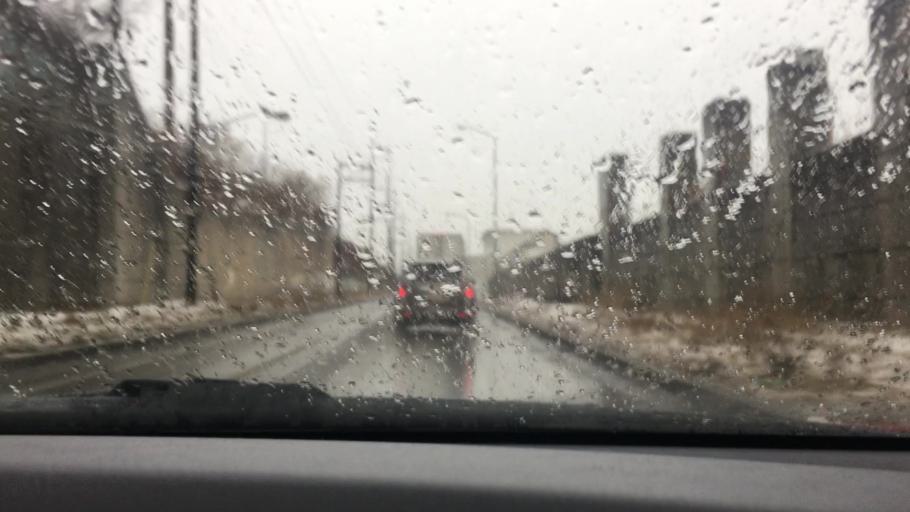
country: US
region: Pennsylvania
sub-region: Allegheny County
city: Mount Oliver
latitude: 40.4186
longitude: -79.9570
